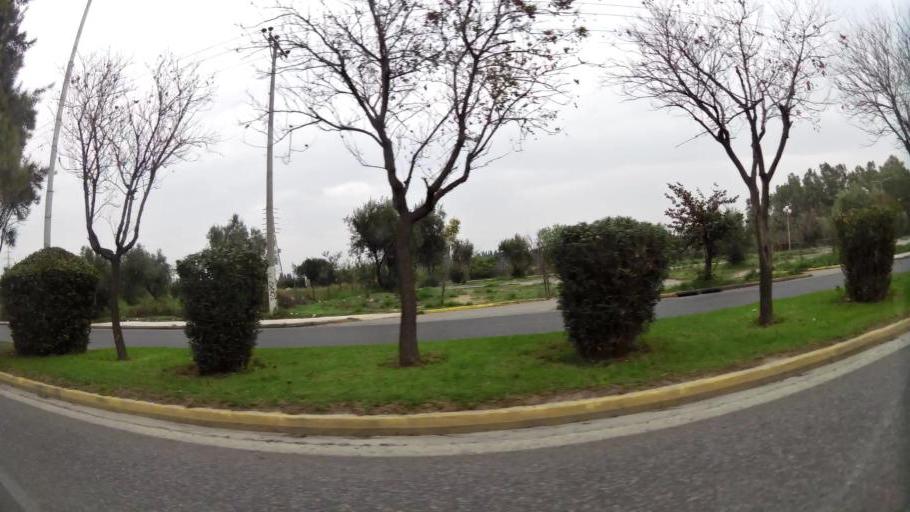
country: GR
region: Attica
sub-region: Nomarchia Athinas
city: Agioi Anargyroi
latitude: 38.0385
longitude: 23.7162
